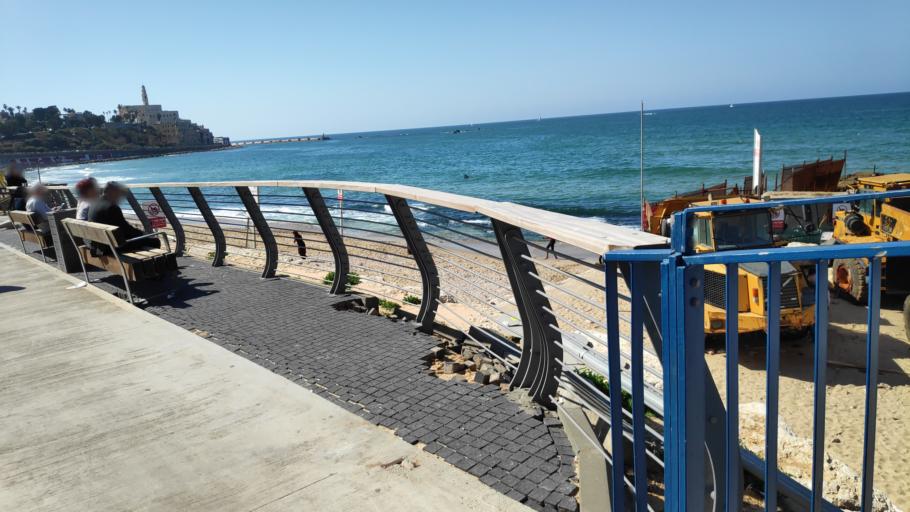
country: IL
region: Tel Aviv
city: Yafo
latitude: 32.0582
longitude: 34.7579
